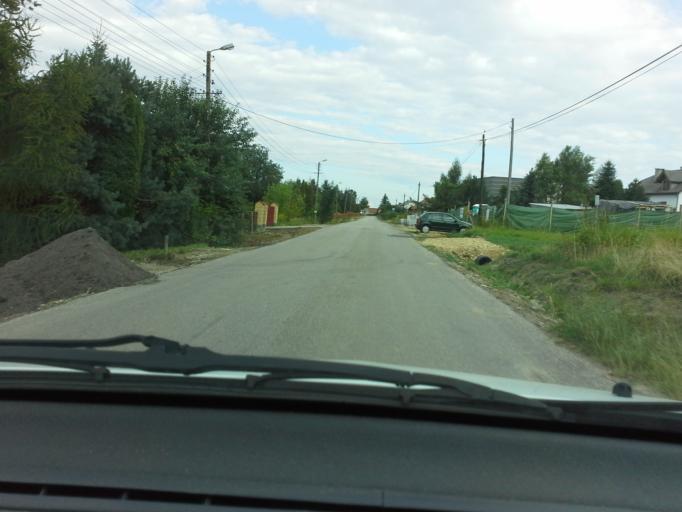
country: PL
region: Lesser Poland Voivodeship
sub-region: Powiat chrzanowski
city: Trzebinia
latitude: 50.1325
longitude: 19.4501
